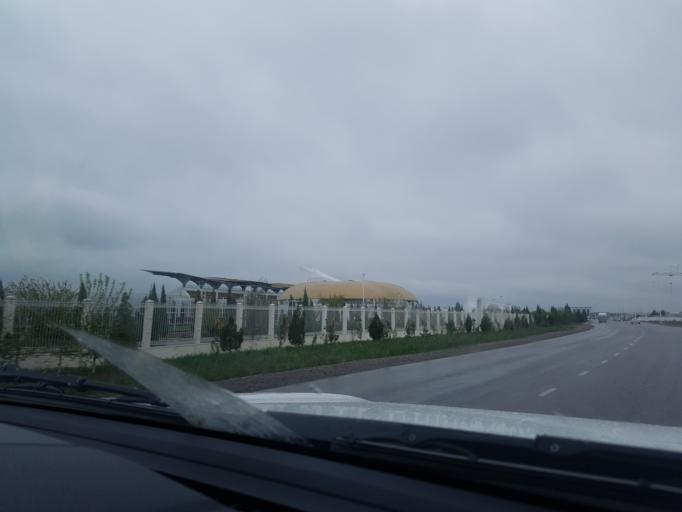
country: TM
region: Lebap
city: Turkmenabat
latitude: 38.9904
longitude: 63.5577
